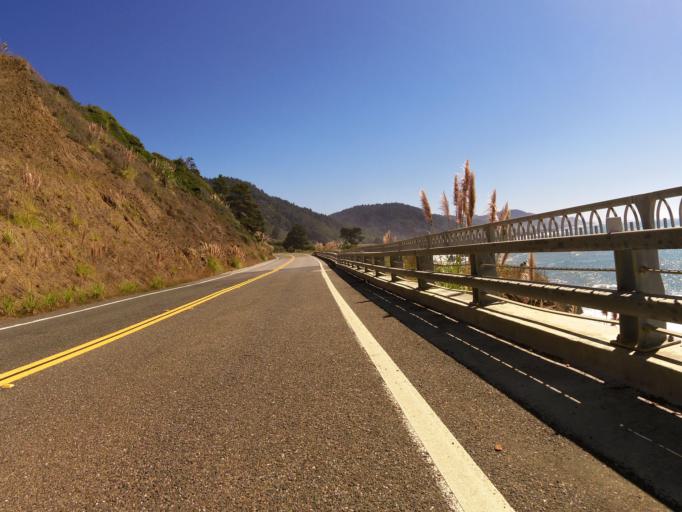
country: US
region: California
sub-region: Mendocino County
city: Fort Bragg
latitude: 39.6942
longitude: -123.7979
